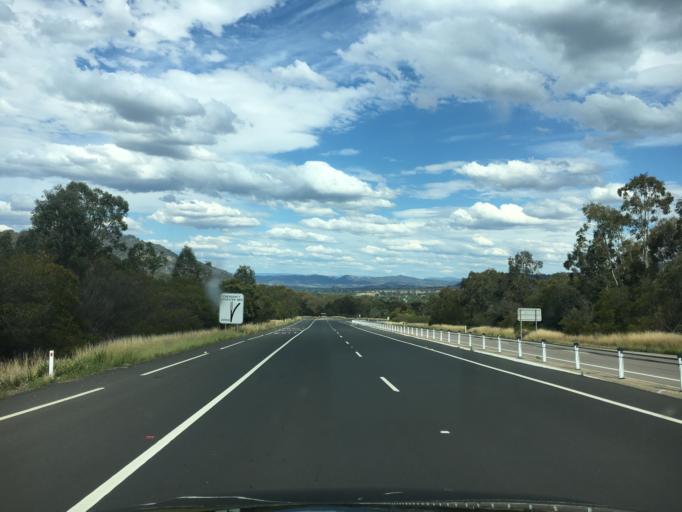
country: AU
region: New South Wales
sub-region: Liverpool Plains
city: Quirindi
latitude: -31.7492
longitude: 150.8094
